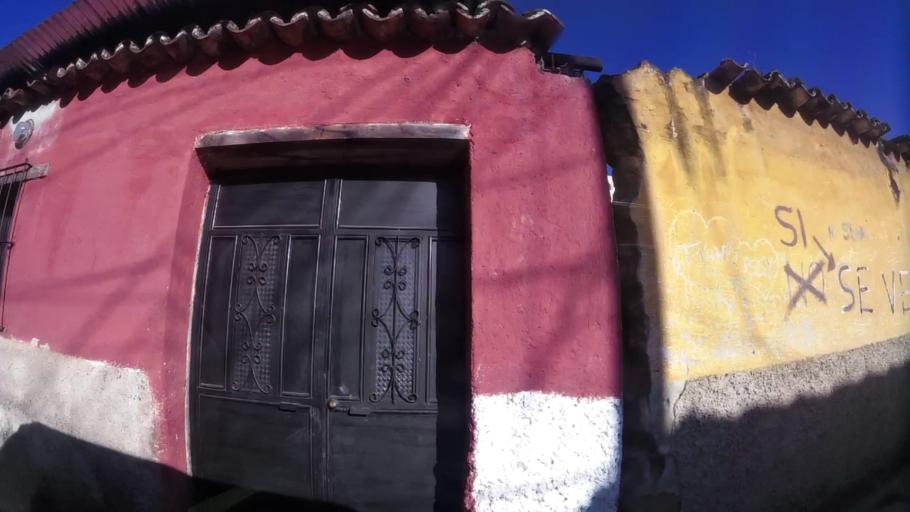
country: GT
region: Sacatepequez
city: Antigua Guatemala
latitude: 14.5539
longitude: -90.7283
